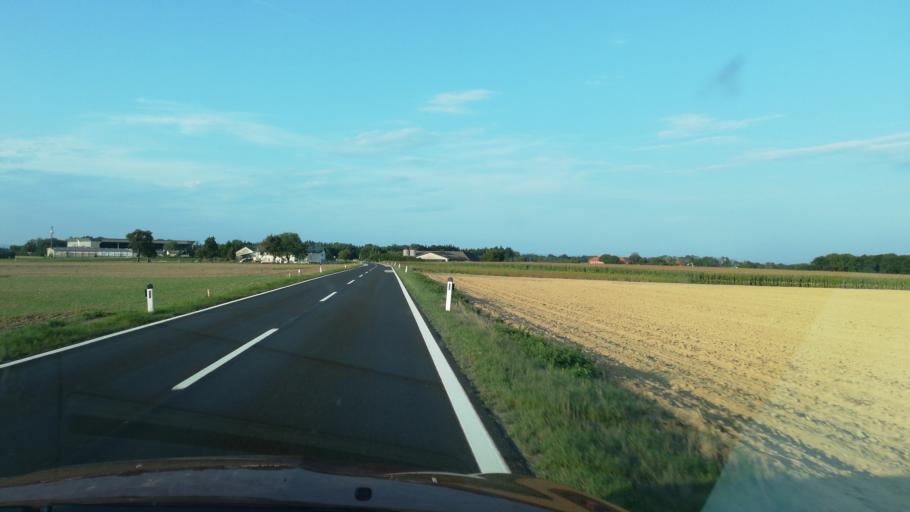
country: AT
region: Upper Austria
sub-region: Politischer Bezirk Steyr-Land
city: Sierning
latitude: 48.1177
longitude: 14.3334
